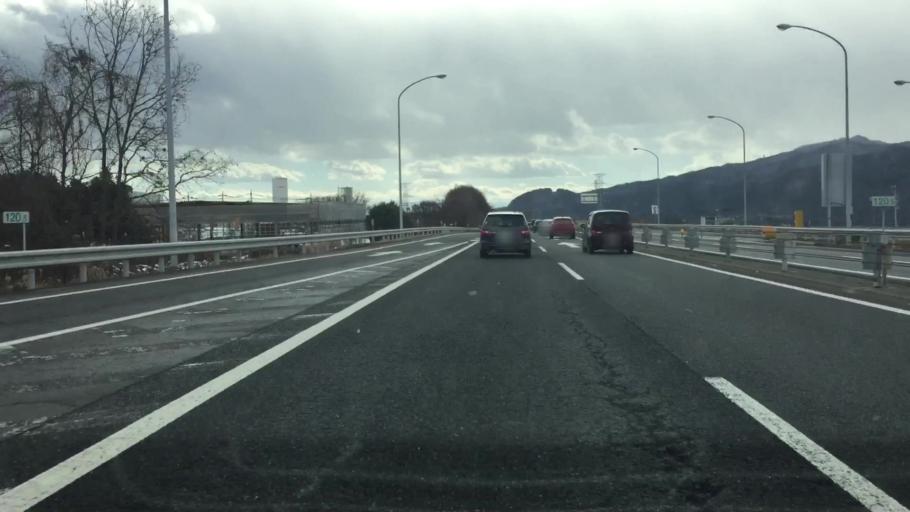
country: JP
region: Gunma
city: Numata
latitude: 36.6145
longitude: 139.0666
